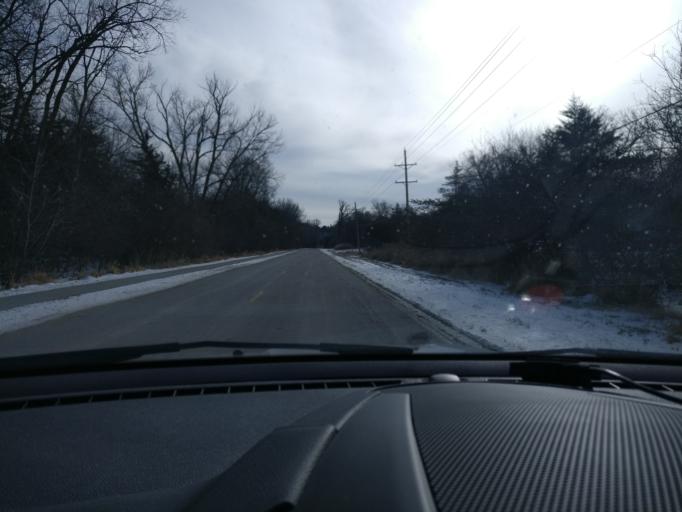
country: US
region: Nebraska
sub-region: Dodge County
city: Fremont
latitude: 41.4178
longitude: -96.5216
